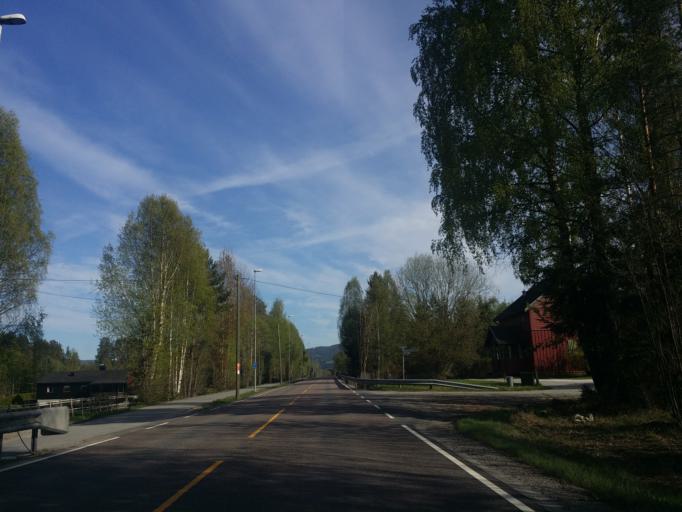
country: NO
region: Telemark
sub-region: Notodden
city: Notodden
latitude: 59.5904
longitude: 9.1535
